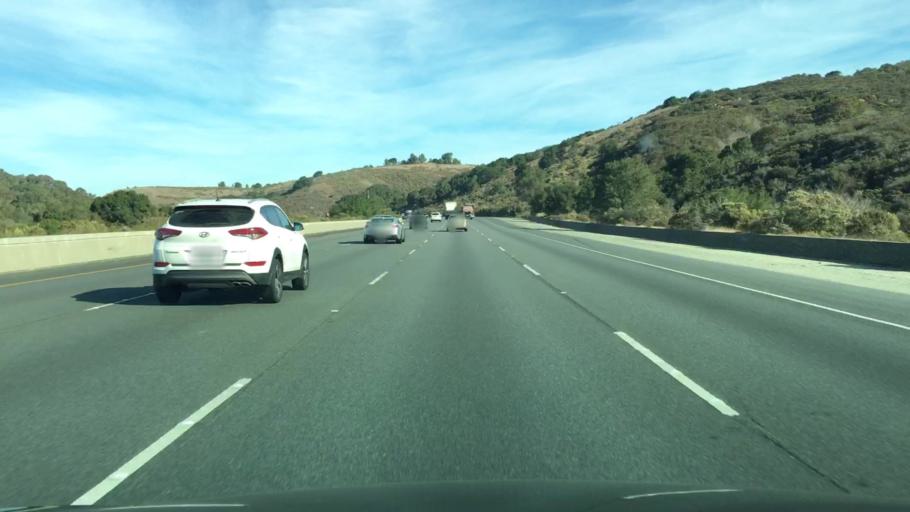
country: US
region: California
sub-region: San Mateo County
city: Emerald Lake Hills
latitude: 37.4841
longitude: -122.2984
